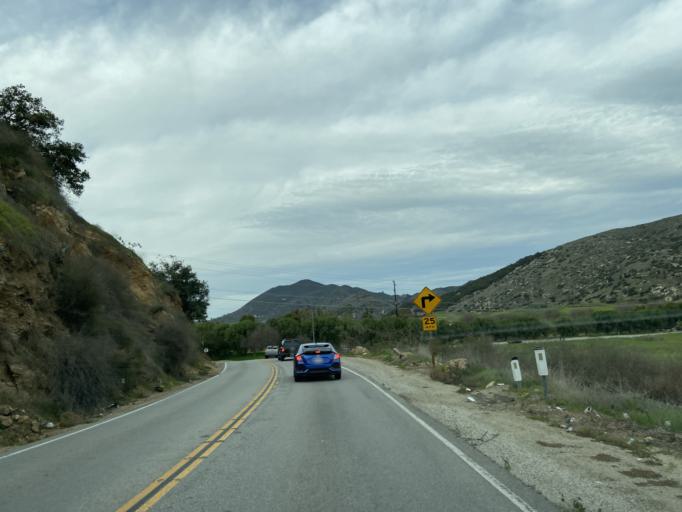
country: US
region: California
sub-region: San Diego County
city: Rainbow
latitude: 33.3420
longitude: -117.1329
